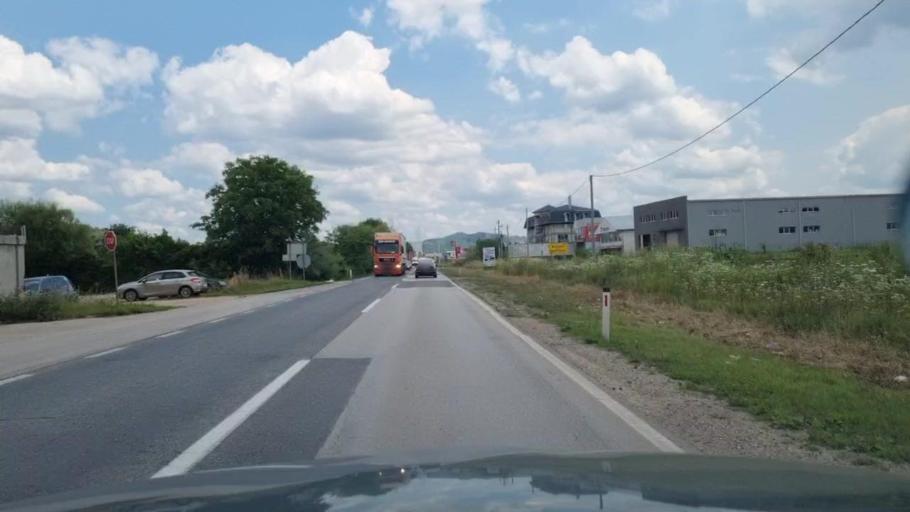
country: BA
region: Federation of Bosnia and Herzegovina
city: Kiseljak
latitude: 44.5140
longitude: 18.5703
